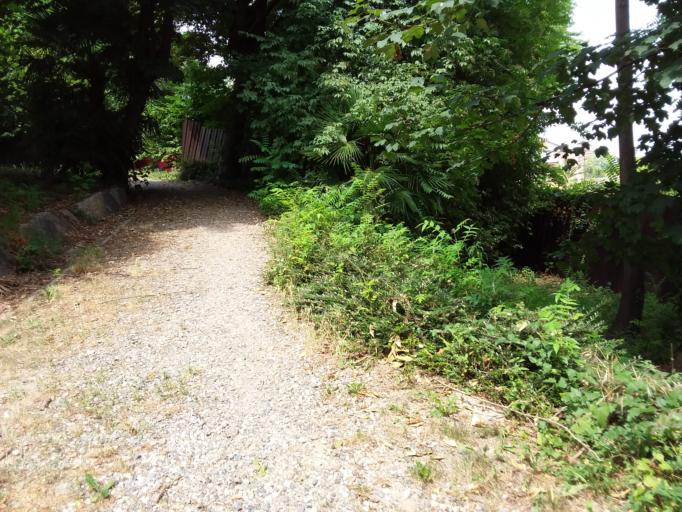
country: IT
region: Piedmont
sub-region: Provincia di Torino
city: Rivoli
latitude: 45.0677
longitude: 7.5070
